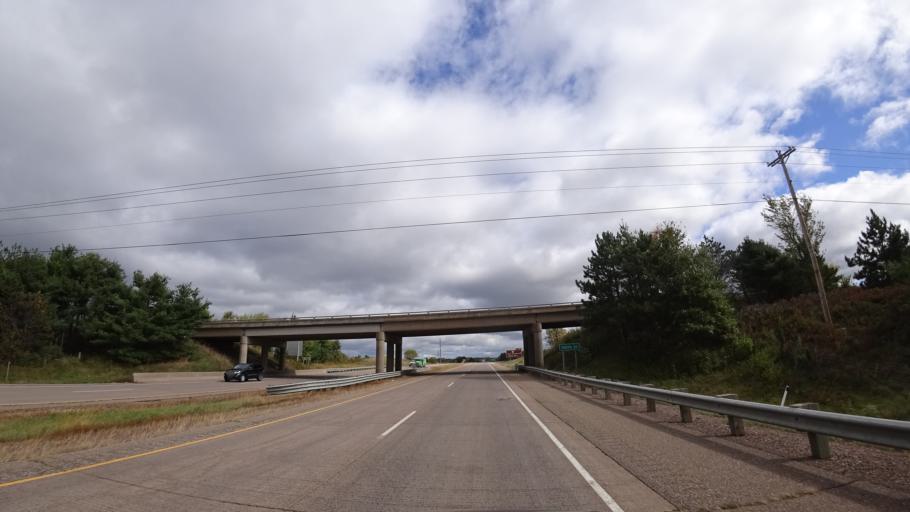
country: US
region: Wisconsin
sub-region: Chippewa County
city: Lake Wissota
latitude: 44.9198
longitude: -91.3478
